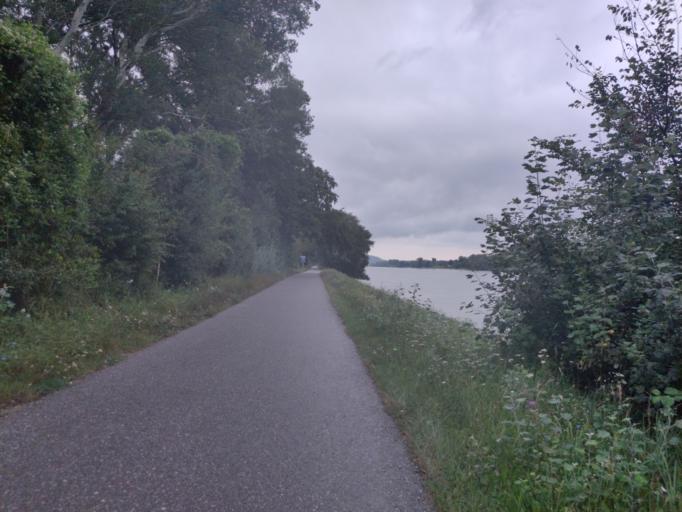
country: AT
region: Lower Austria
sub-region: Politischer Bezirk Korneuburg
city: Leobendorf
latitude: 48.3516
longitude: 16.2895
